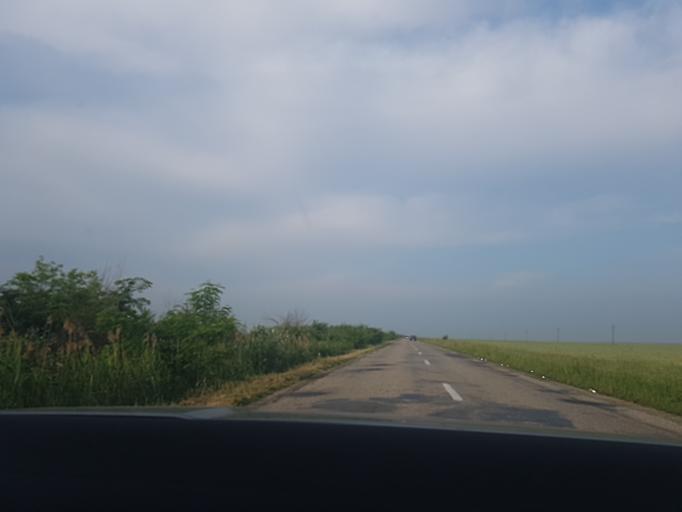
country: RO
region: Timis
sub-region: Comuna Giulvaz
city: Giulvaz
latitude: 45.5765
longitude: 21.0174
